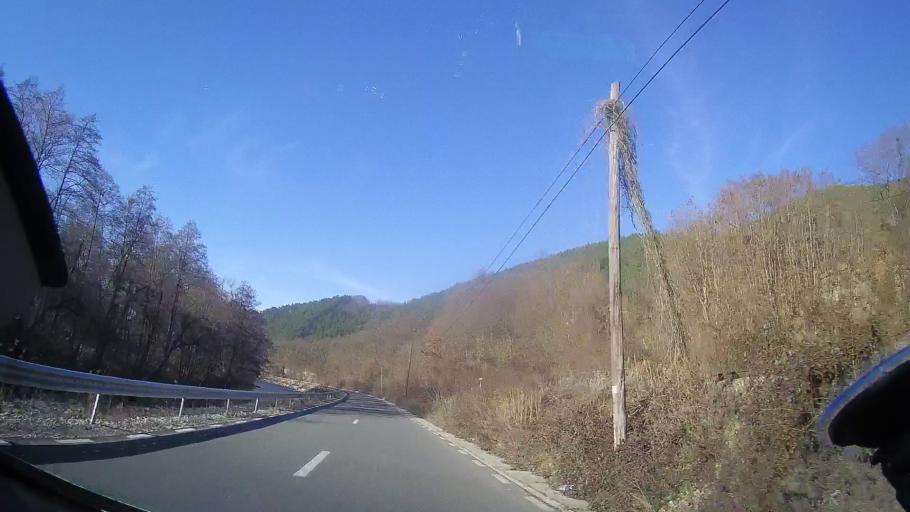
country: RO
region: Bihor
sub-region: Comuna Bratca
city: Bratca
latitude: 46.9284
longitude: 22.6459
